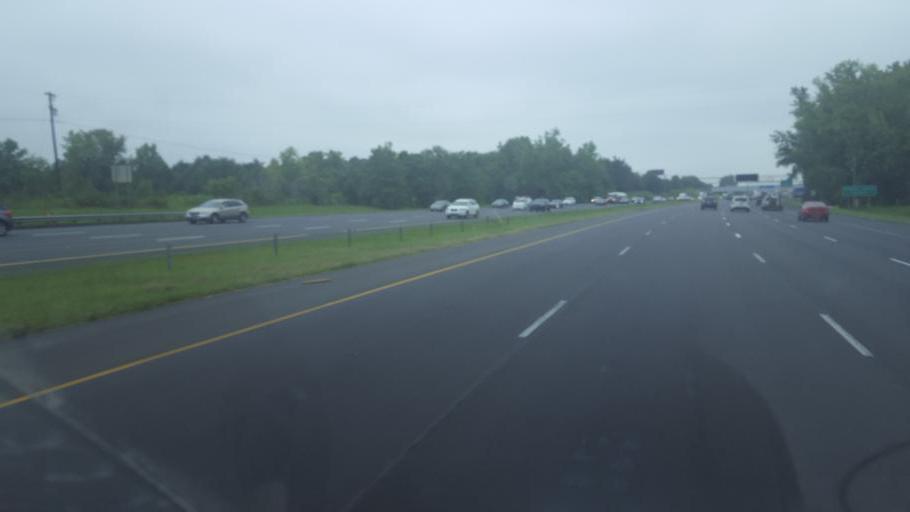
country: US
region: North Carolina
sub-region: Mecklenburg County
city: Pineville
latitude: 35.1043
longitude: -80.9306
